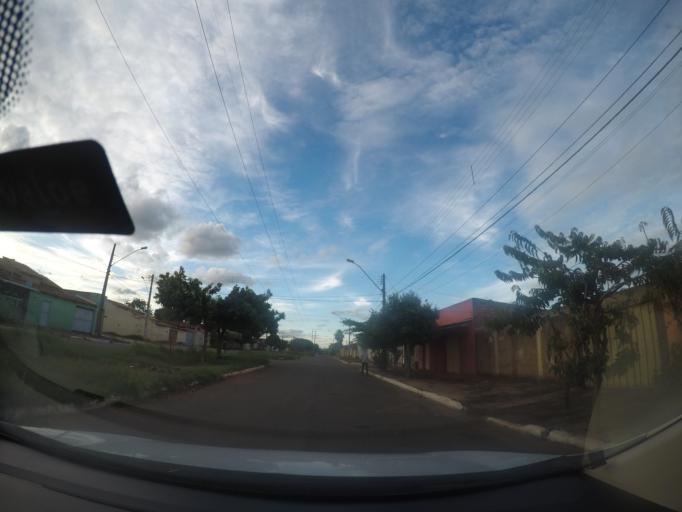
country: BR
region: Goias
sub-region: Goianira
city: Goianira
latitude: -16.5877
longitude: -49.3767
